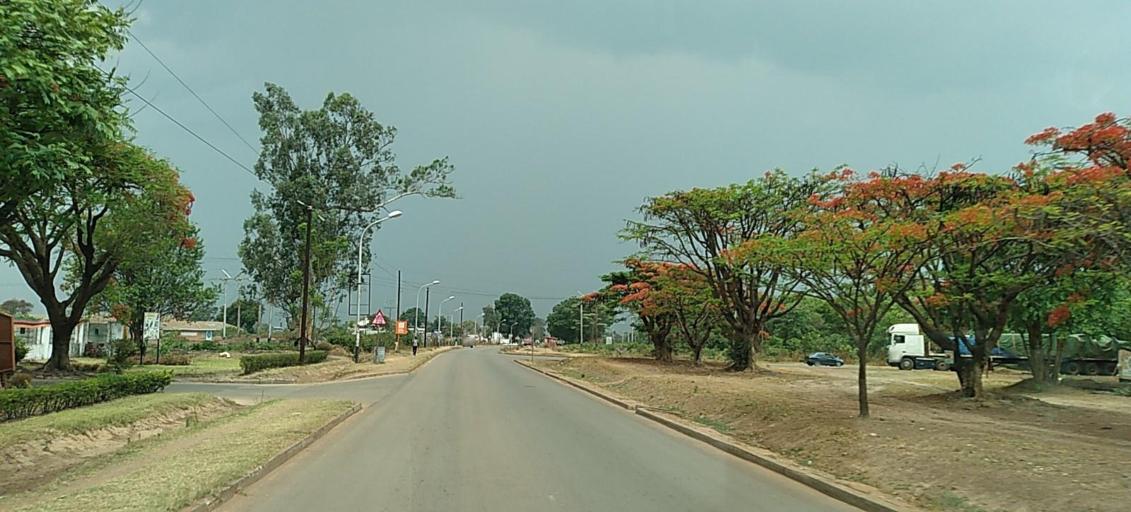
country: ZM
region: Copperbelt
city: Kalulushi
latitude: -12.8326
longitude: 28.1017
